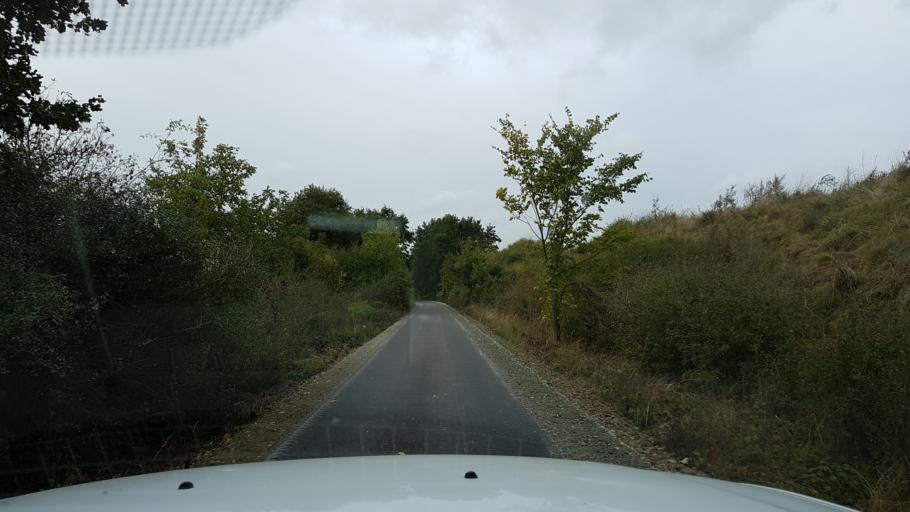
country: PL
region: West Pomeranian Voivodeship
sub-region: Powiat gryfinski
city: Moryn
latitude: 52.8746
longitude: 14.3839
